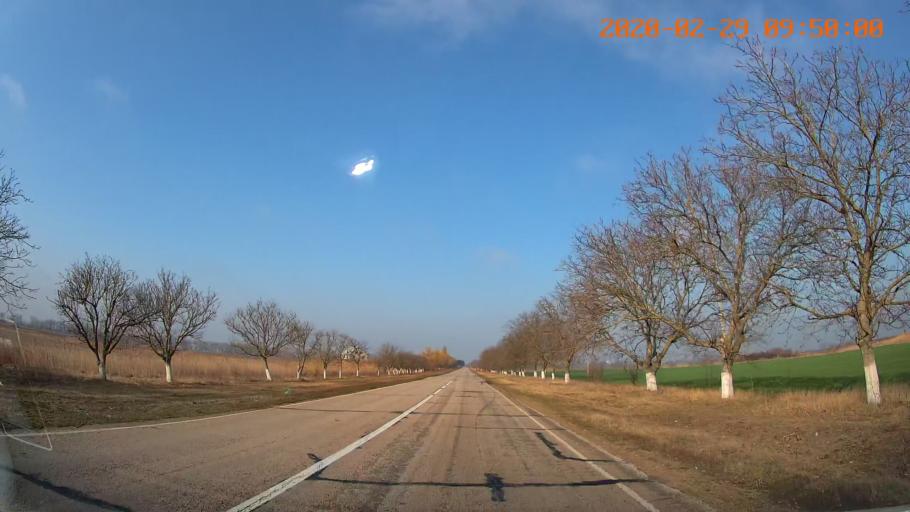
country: MD
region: Telenesti
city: Slobozia
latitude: 46.7008
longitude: 29.7636
